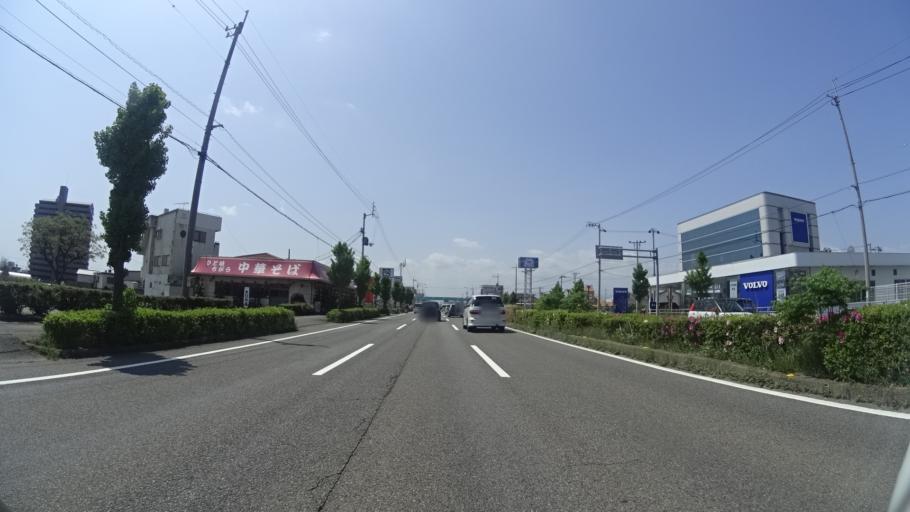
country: JP
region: Tokushima
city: Tokushima-shi
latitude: 34.1144
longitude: 134.5777
